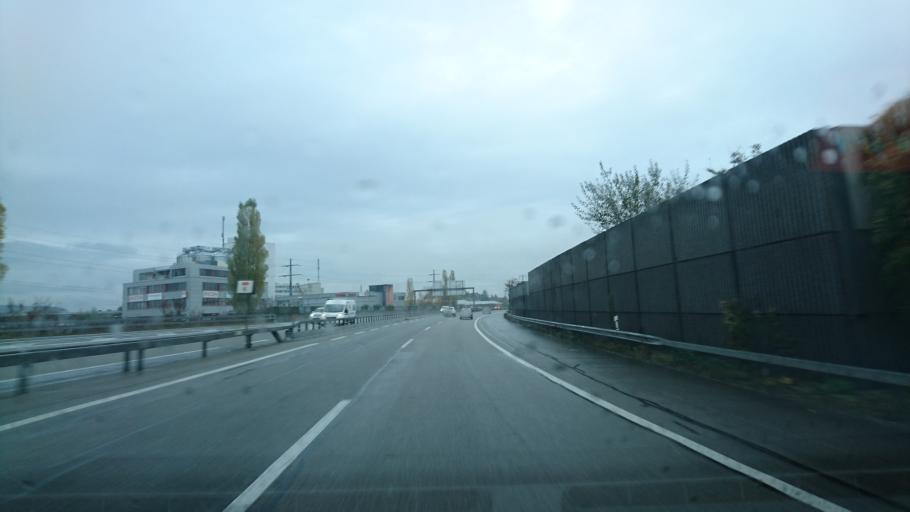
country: CH
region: Bern
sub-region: Bern-Mittelland District
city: Urtenen
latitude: 47.0152
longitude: 7.4967
